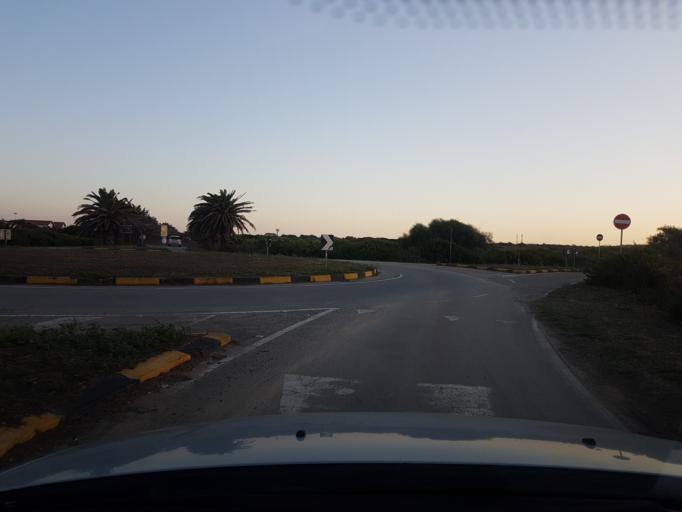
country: IT
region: Sardinia
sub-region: Provincia di Oristano
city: Riola Sardo
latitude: 40.0409
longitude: 8.4018
